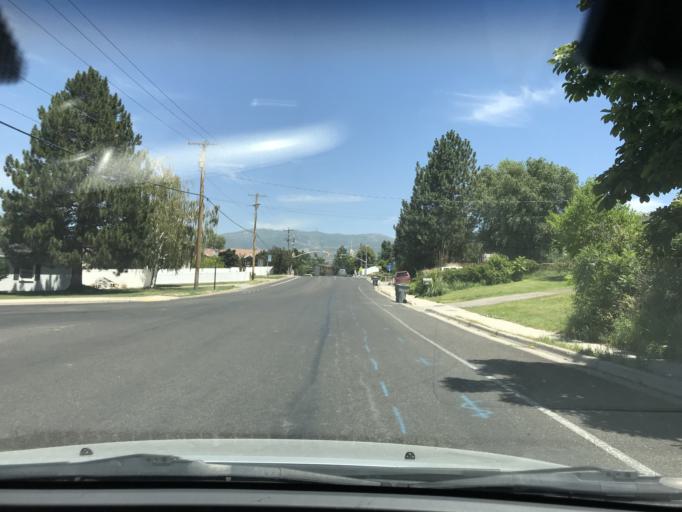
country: US
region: Utah
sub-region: Davis County
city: North Salt Lake
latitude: 40.8483
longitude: -111.8978
